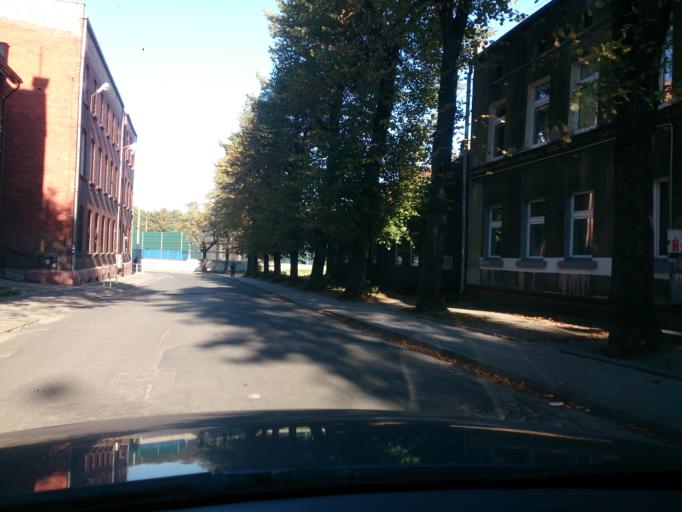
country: PL
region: Pomeranian Voivodeship
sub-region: Gdansk
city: Gdansk
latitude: 54.3231
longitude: 18.6332
